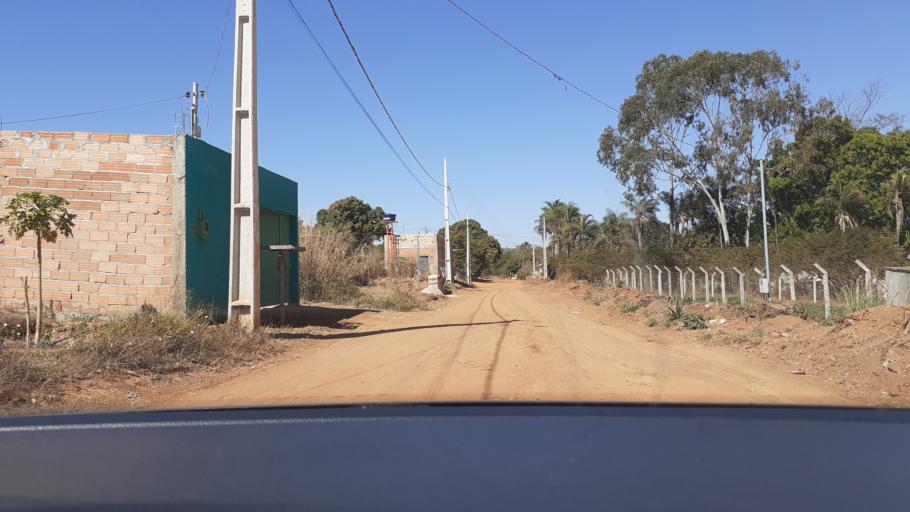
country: BR
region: Goias
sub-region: Aparecida De Goiania
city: Aparecida de Goiania
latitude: -16.8812
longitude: -49.2609
